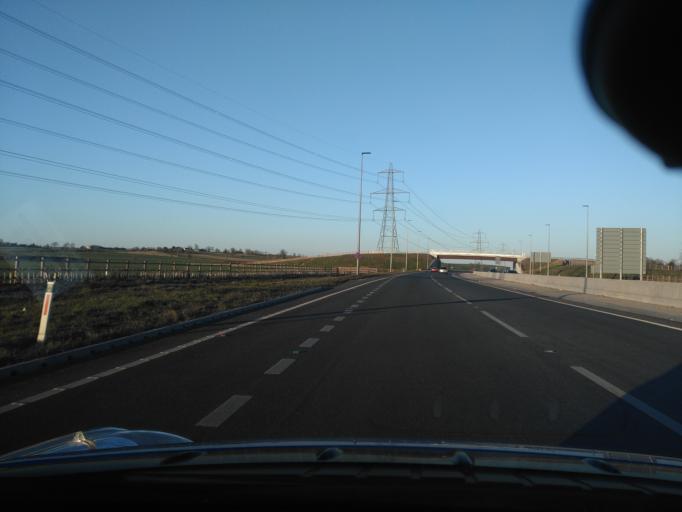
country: GB
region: England
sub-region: Central Bedfordshire
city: Houghton Regis
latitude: 51.9115
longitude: -0.5514
